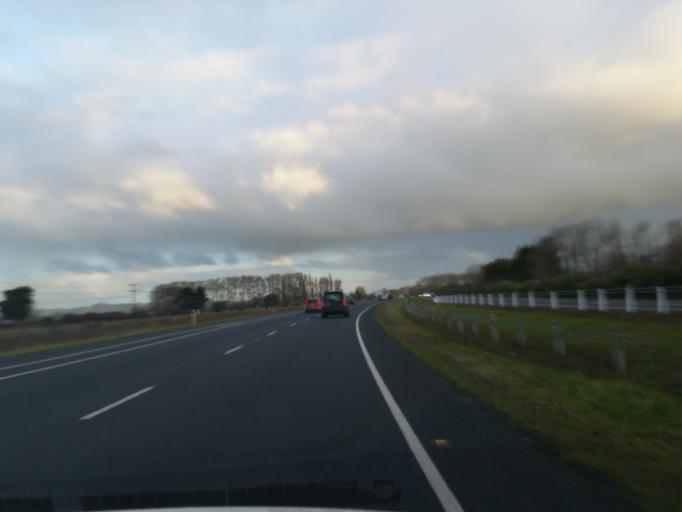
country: NZ
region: Waikato
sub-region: Waikato District
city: Te Kauwhata
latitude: -37.4452
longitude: 175.1517
